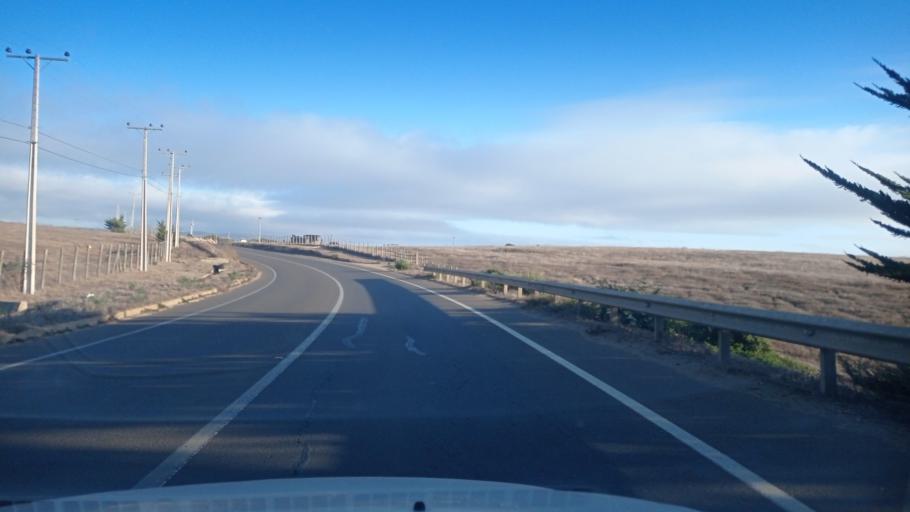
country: CL
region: O'Higgins
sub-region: Provincia de Colchagua
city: Santa Cruz
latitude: -34.4409
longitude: -72.0329
